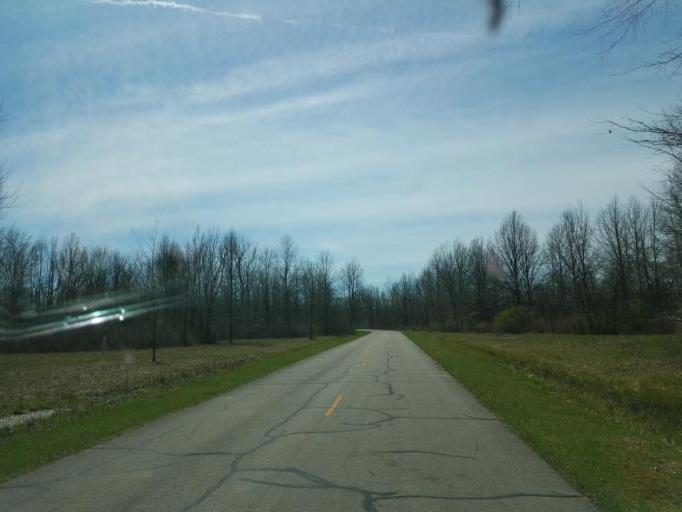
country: US
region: Ohio
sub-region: Delaware County
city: Delaware
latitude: 40.4025
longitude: -83.0632
